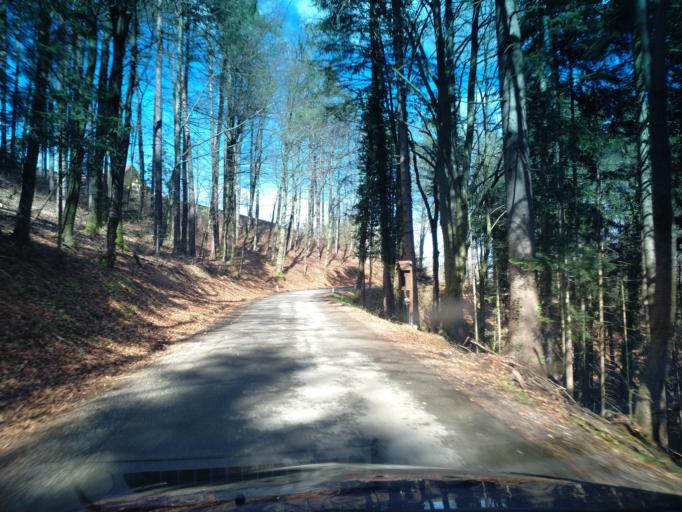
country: AT
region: Styria
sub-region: Politischer Bezirk Leibnitz
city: Sankt Johann im Saggautal
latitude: 46.7175
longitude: 15.3852
